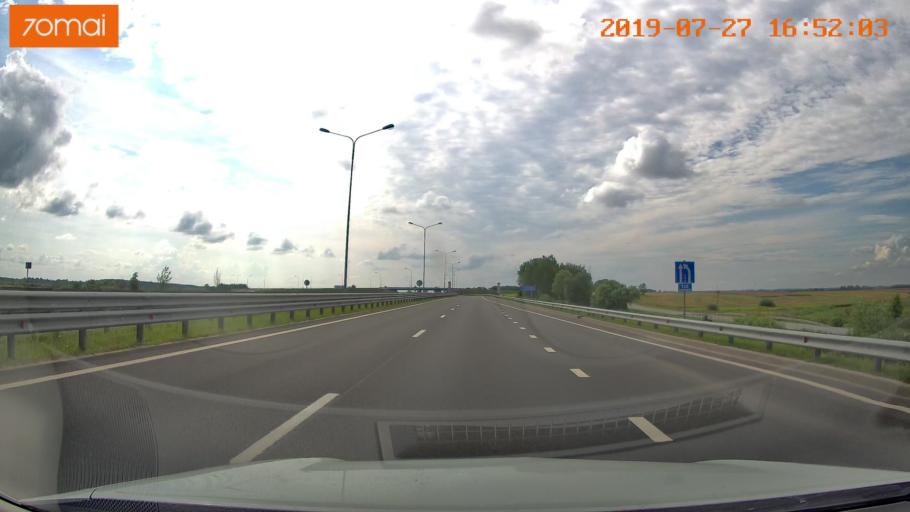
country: RU
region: Kaliningrad
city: Gvardeysk
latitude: 54.6841
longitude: 20.8709
